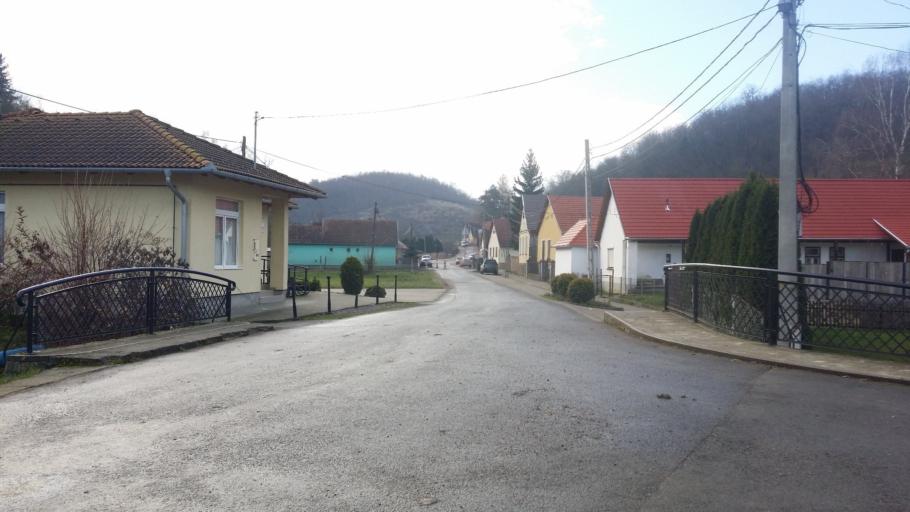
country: HU
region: Tolna
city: Bonyhad
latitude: 46.2214
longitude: 18.5988
